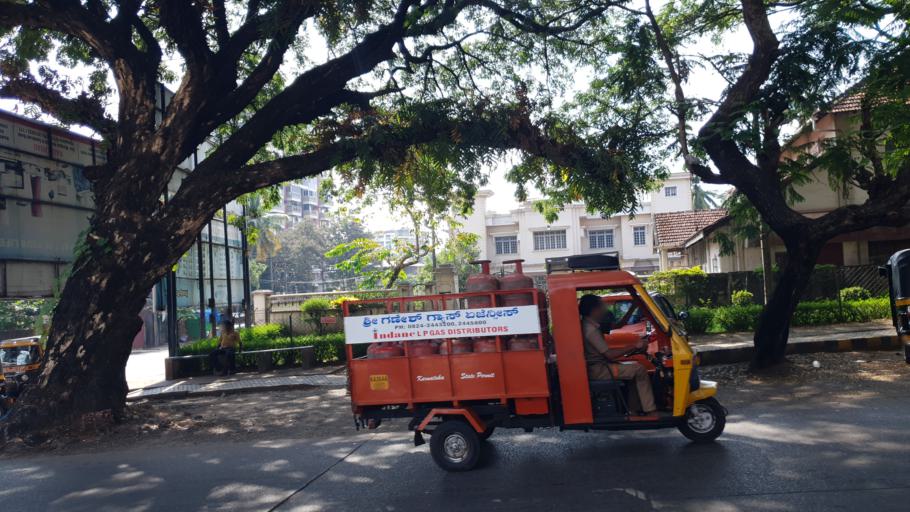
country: IN
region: Karnataka
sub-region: Dakshina Kannada
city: Mangalore
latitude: 12.8829
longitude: 74.8393
